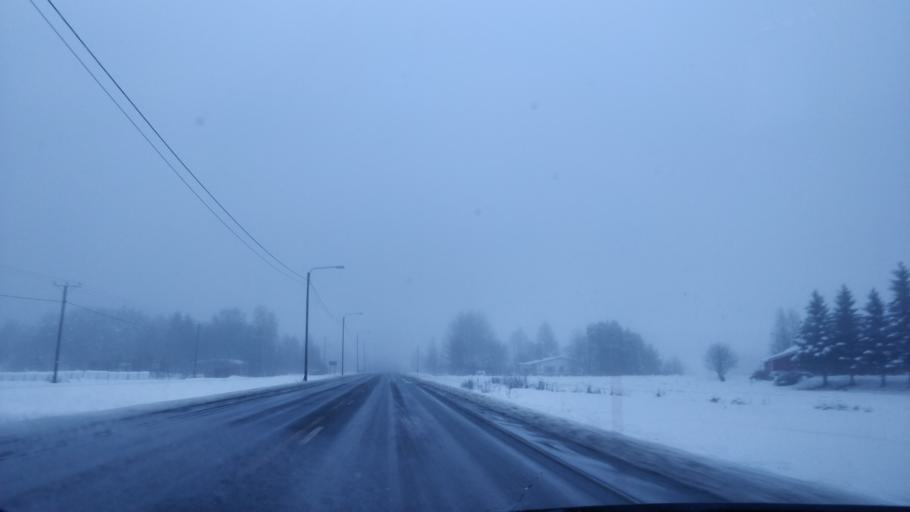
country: FI
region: Lapland
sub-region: Kemi-Tornio
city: Tervola
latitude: 66.1464
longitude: 24.9662
